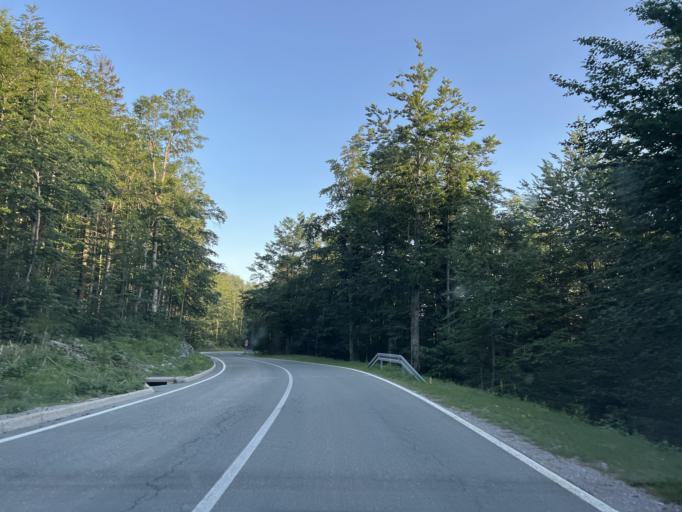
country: HR
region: Primorsko-Goranska
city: Podhum
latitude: 45.4181
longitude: 14.5647
